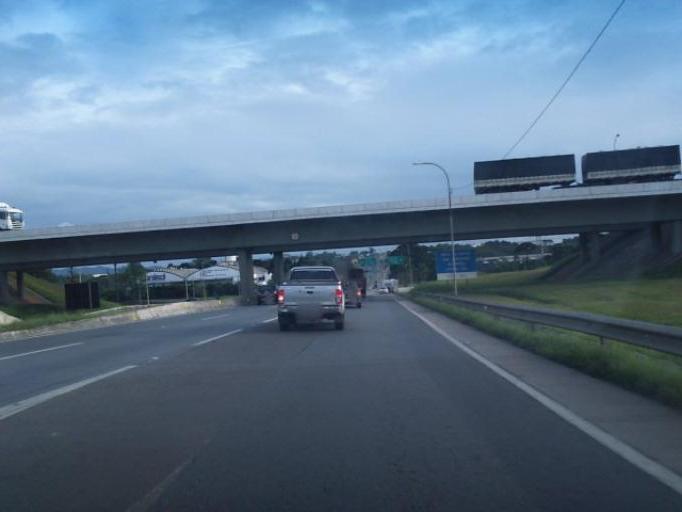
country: BR
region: Parana
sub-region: Sao Jose Dos Pinhais
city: Sao Jose dos Pinhais
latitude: -25.5686
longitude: -49.1821
